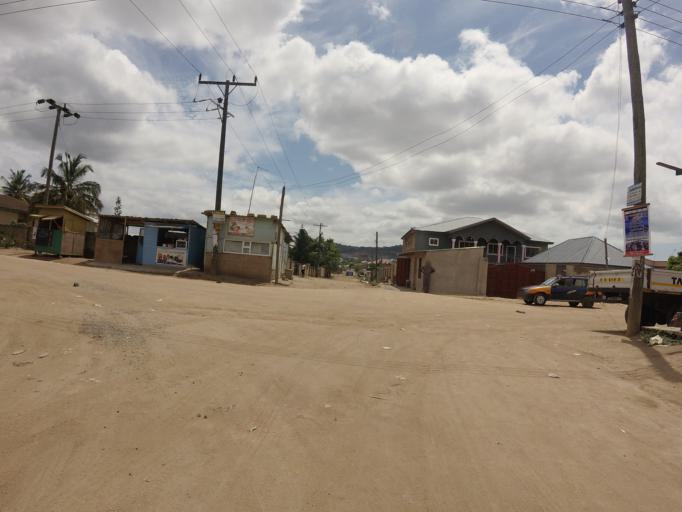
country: GH
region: Central
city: Kasoa
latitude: 5.5445
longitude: -0.3977
